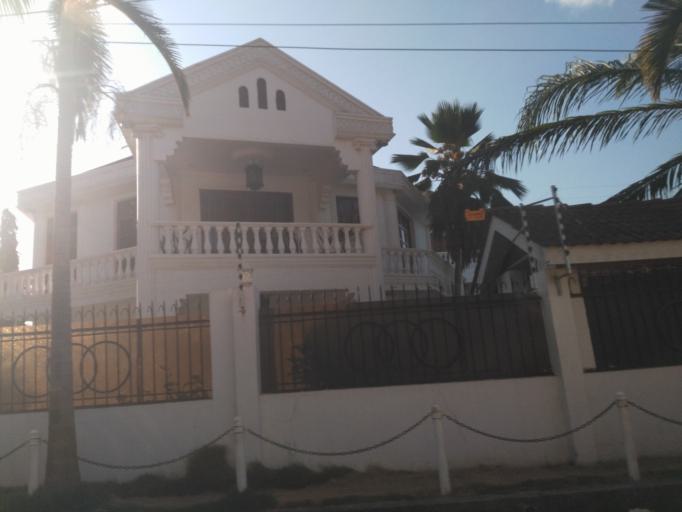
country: TZ
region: Dar es Salaam
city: Magomeni
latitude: -6.7651
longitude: 39.2547
